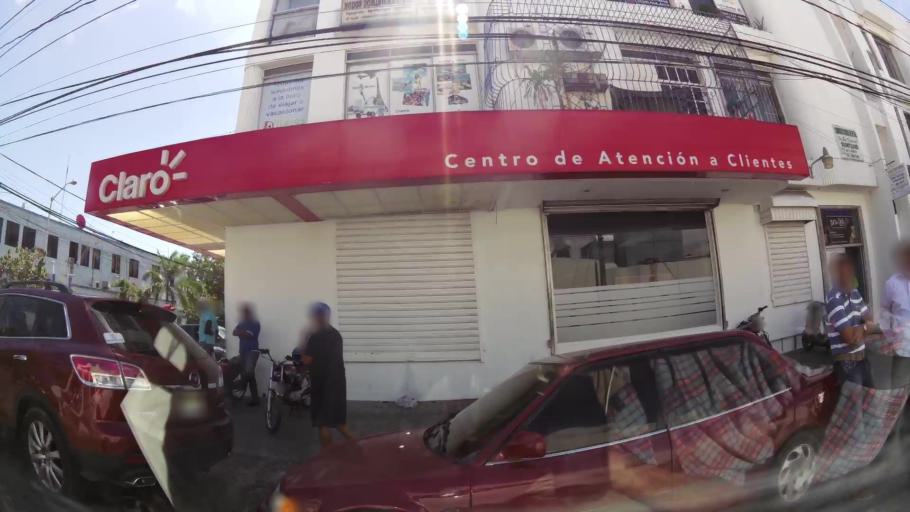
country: DO
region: San Cristobal
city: San Cristobal
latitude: 18.4154
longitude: -70.1103
